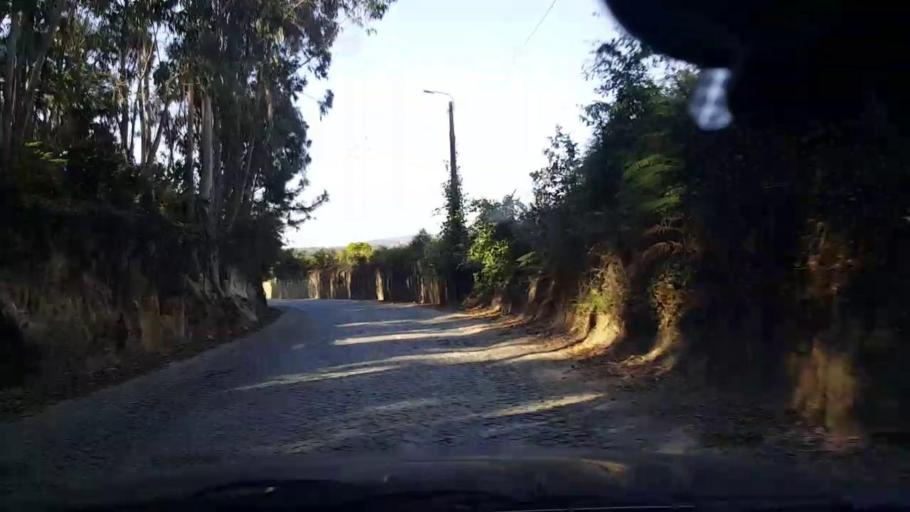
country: PT
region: Porto
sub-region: Vila do Conde
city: Arvore
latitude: 41.3566
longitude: -8.7087
